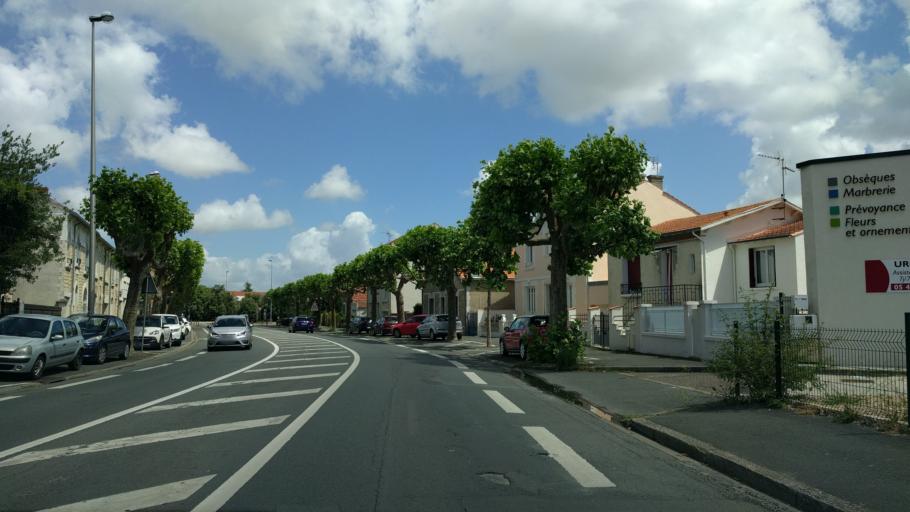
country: FR
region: Poitou-Charentes
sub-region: Departement de la Charente-Maritime
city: La Rochelle
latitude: 46.1619
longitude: -1.1394
